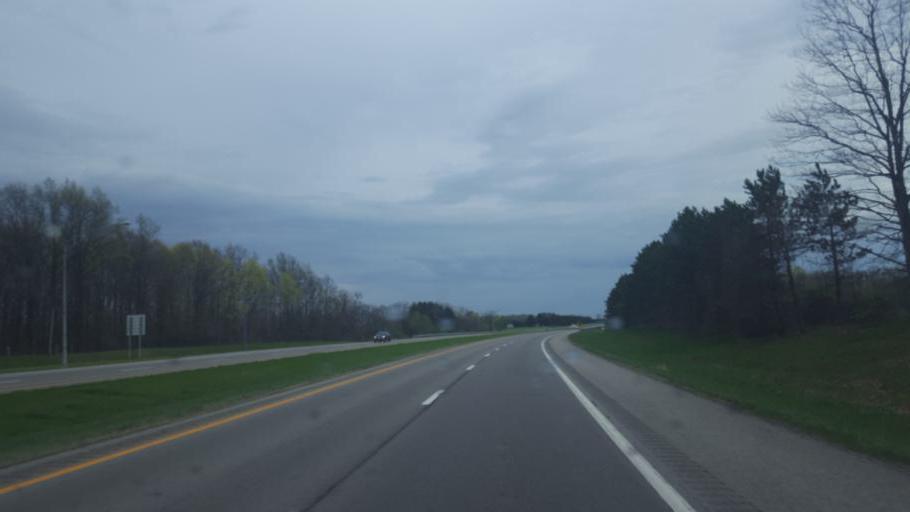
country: US
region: Ohio
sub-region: Wyandot County
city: Carey
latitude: 40.9204
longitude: -83.3566
